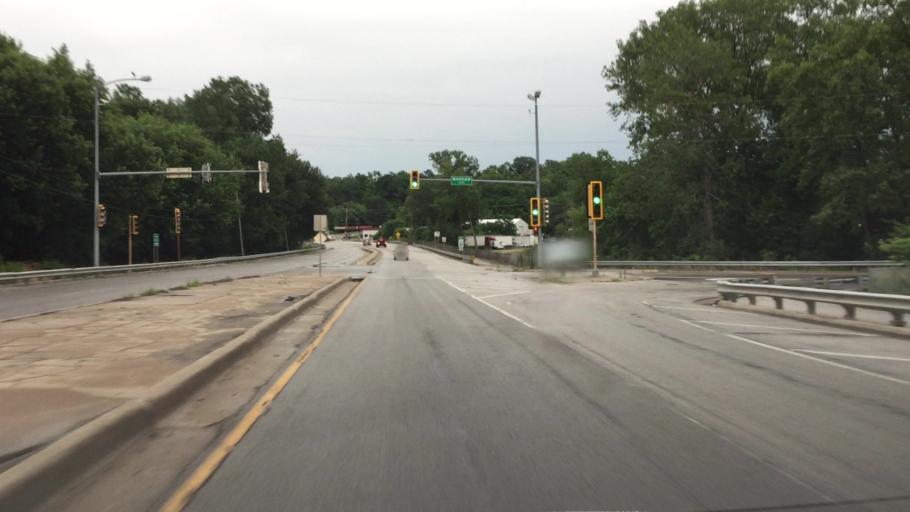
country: US
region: Illinois
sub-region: Hancock County
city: Hamilton
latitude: 40.3900
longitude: -91.3600
